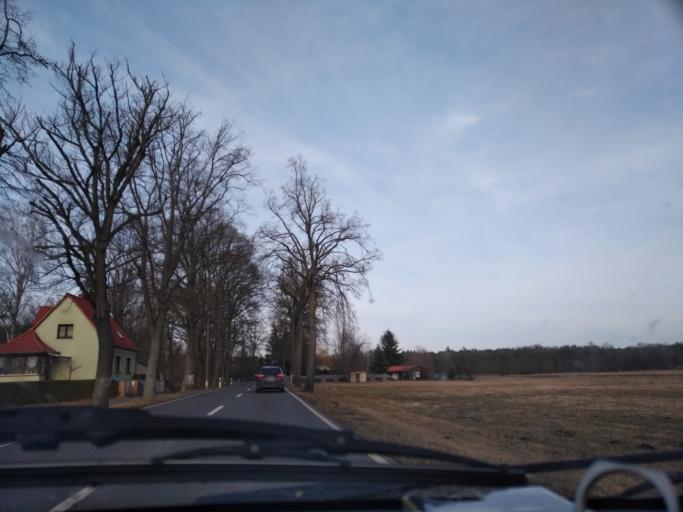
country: DE
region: Brandenburg
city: Luckenwalde
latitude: 52.1064
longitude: 13.1926
